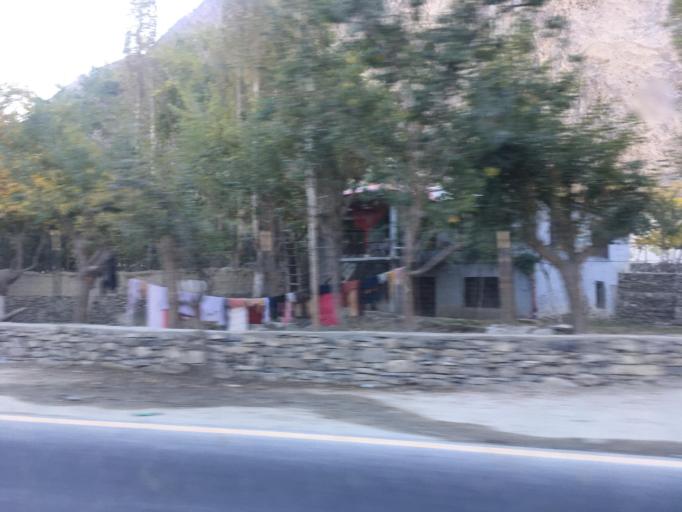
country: PK
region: Gilgit-Baltistan
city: Skardu
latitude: 35.3599
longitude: 75.5079
